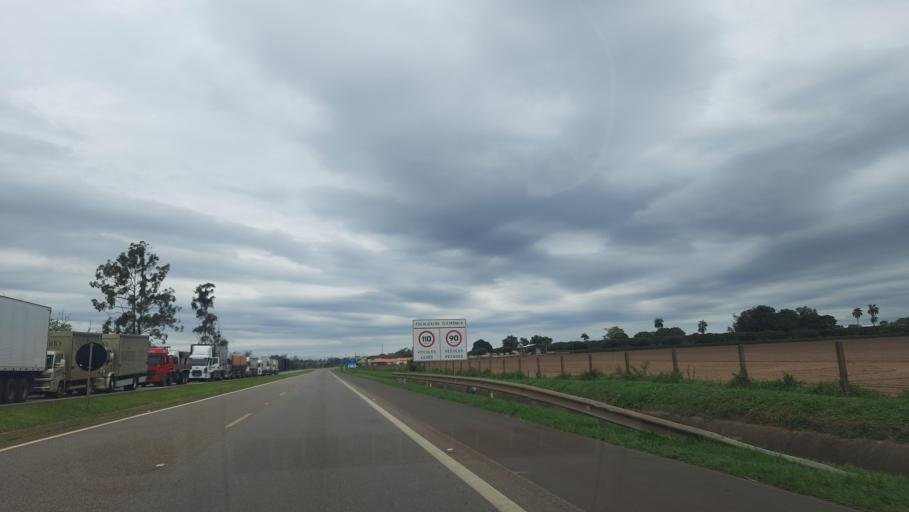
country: BR
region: Sao Paulo
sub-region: Casa Branca
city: Casa Branca
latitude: -21.7914
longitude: -47.0626
